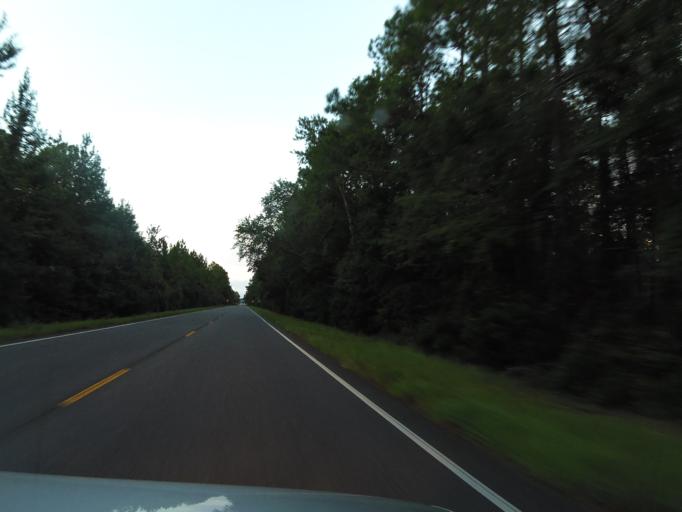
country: US
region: Georgia
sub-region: Camden County
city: Kingsland
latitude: 30.7521
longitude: -81.6876
